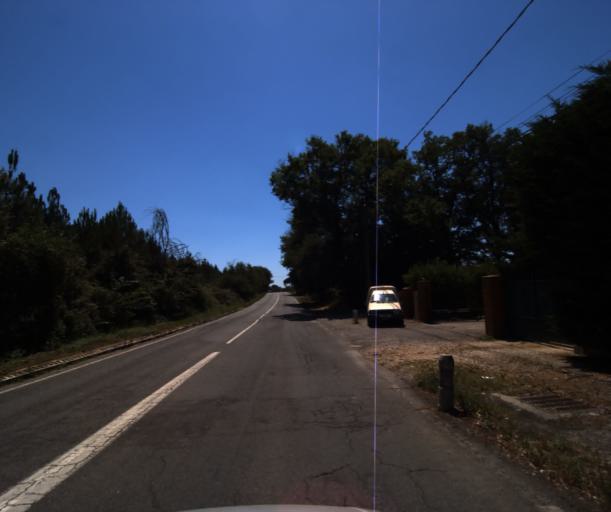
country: FR
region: Midi-Pyrenees
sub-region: Departement de la Haute-Garonne
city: Seysses
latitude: 43.4637
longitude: 1.2987
